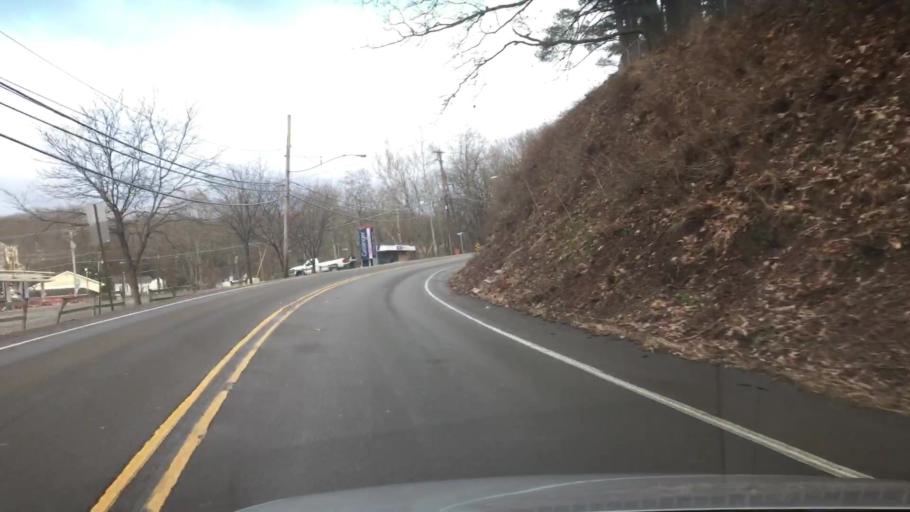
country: US
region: Pennsylvania
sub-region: Columbia County
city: Bloomsburg
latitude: 41.0066
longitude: -76.4500
